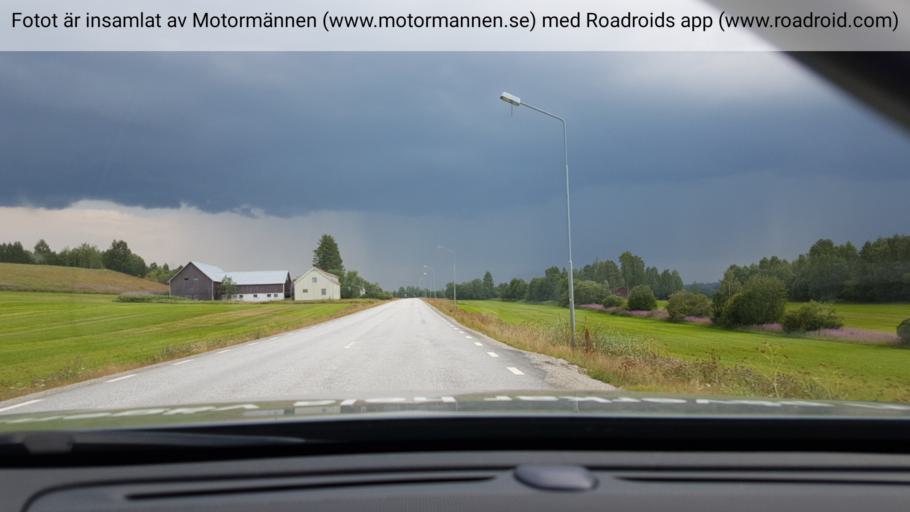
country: SE
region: Vaesterbotten
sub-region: Vindelns Kommun
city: Vindeln
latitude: 64.1721
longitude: 19.4873
